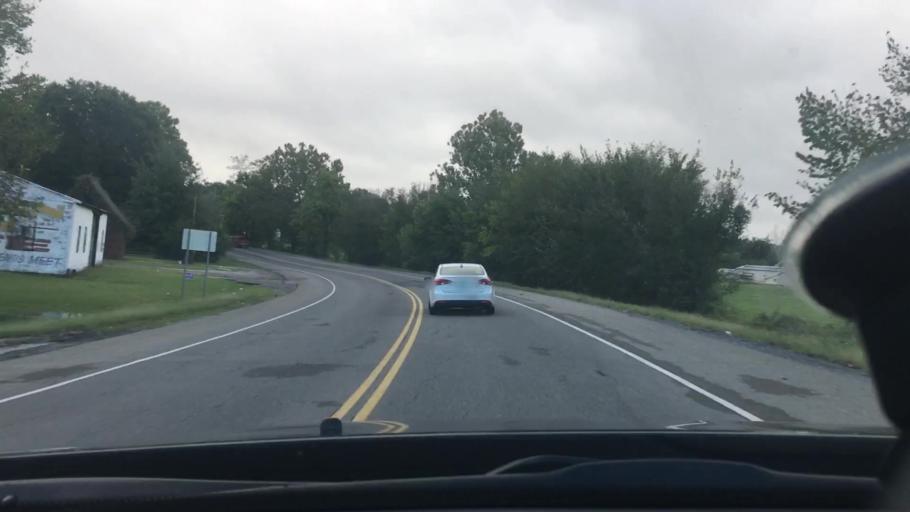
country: US
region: Oklahoma
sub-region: Coal County
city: Coalgate
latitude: 34.5424
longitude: -96.2275
